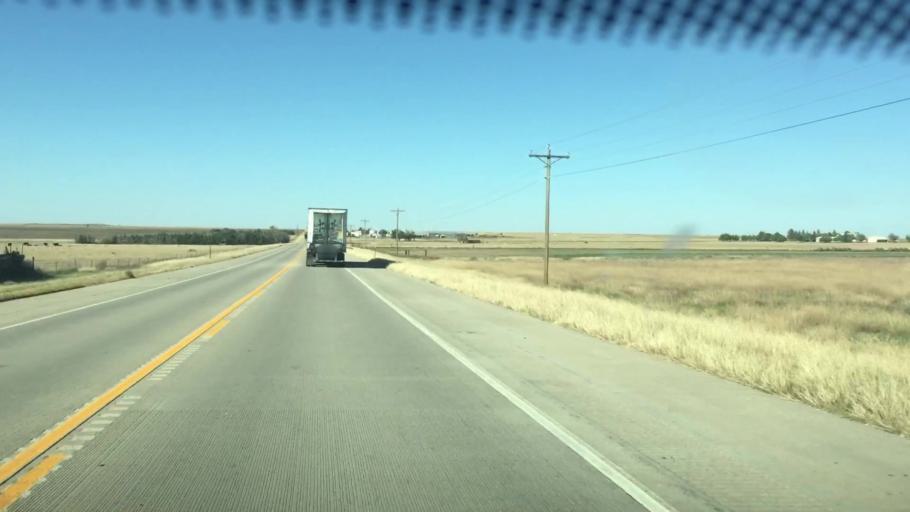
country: US
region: Colorado
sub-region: Kiowa County
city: Eads
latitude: 38.4553
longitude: -102.7306
